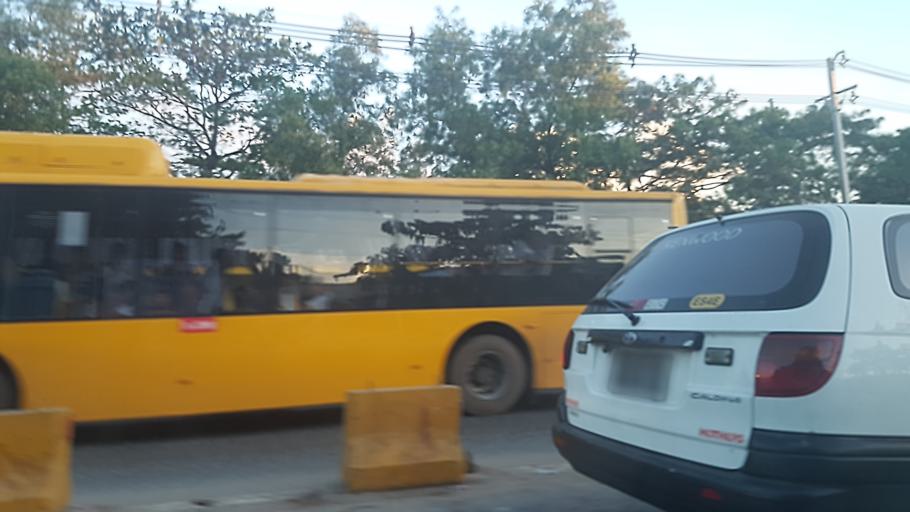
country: MM
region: Yangon
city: Yangon
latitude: 16.8941
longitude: 96.1206
